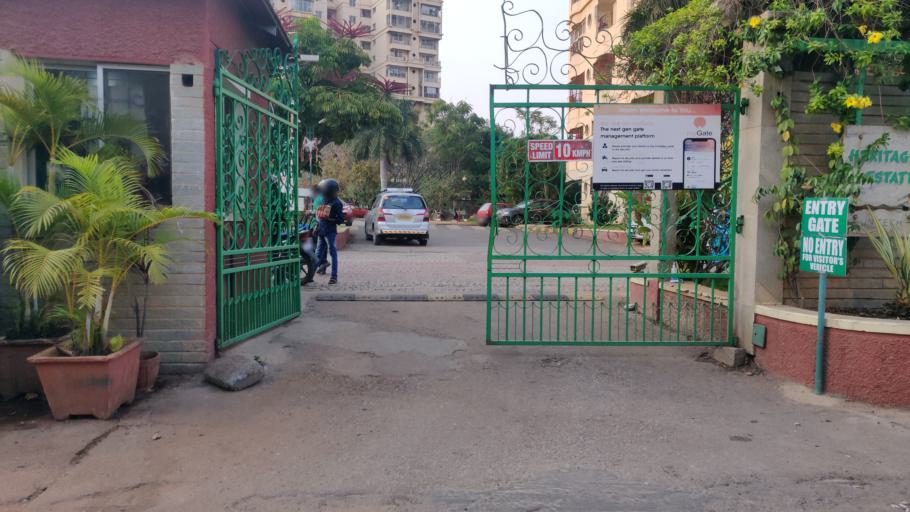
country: IN
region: Karnataka
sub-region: Bangalore Urban
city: Yelahanka
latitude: 13.1187
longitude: 77.5799
